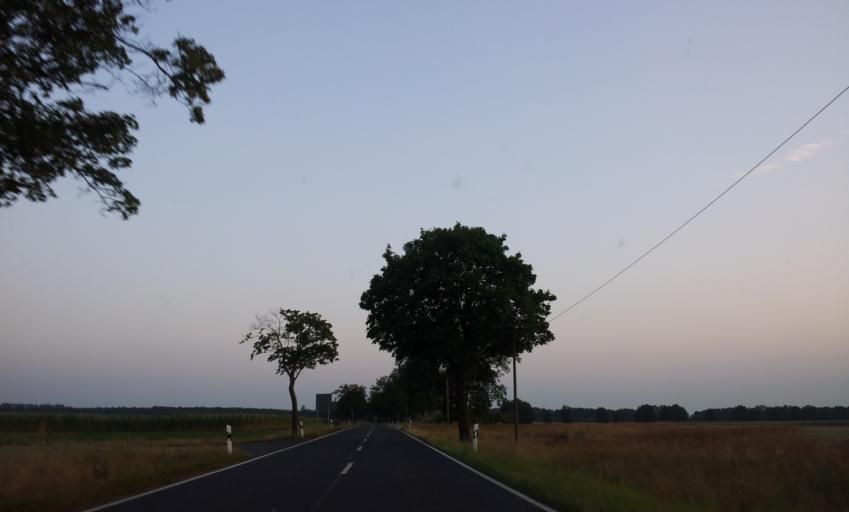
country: DE
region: Brandenburg
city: Beelitz
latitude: 52.1341
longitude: 12.9880
